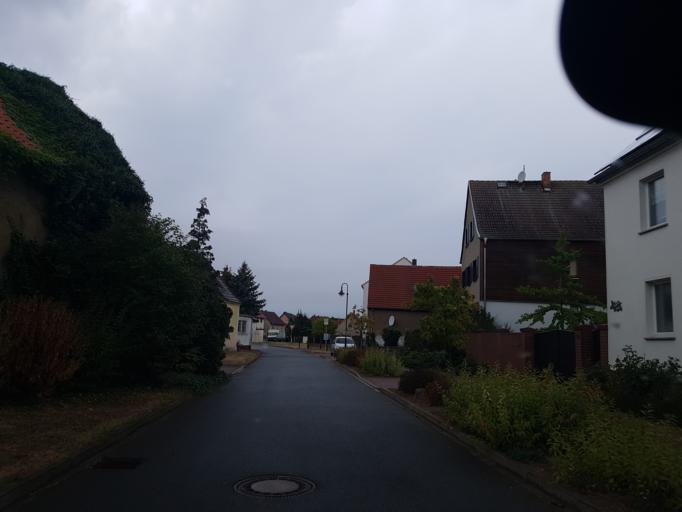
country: DE
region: Saxony-Anhalt
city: Jessen
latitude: 51.7683
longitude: 12.9032
